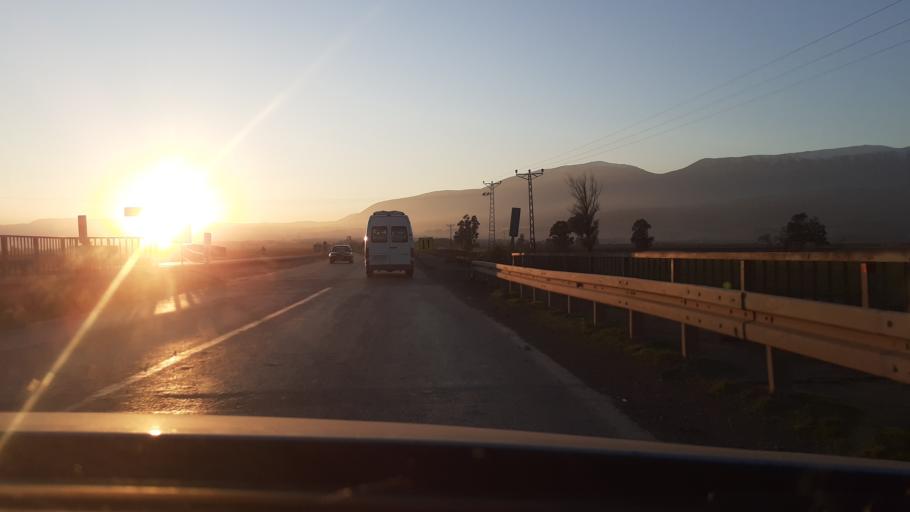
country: TR
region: Hatay
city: Kirikhan
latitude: 36.5047
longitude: 36.4120
